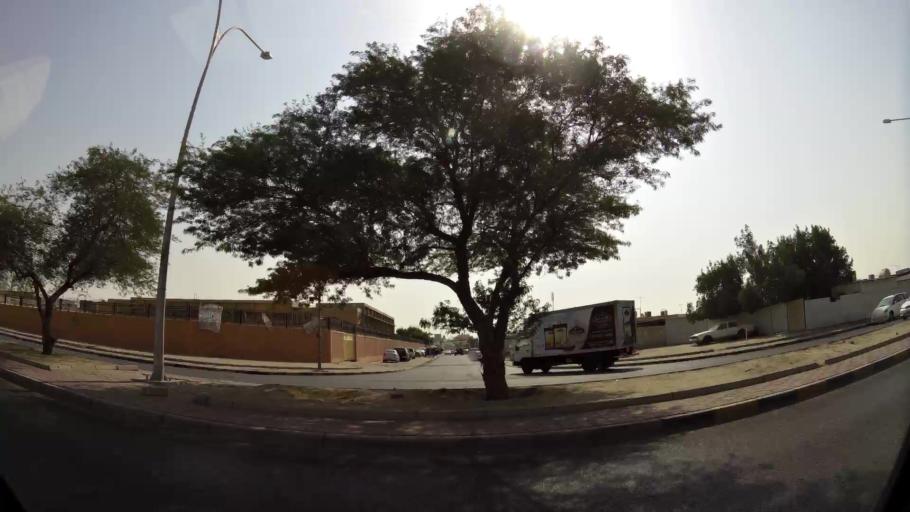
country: KW
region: Muhafazat al Jahra'
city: Al Jahra'
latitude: 29.3303
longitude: 47.6760
